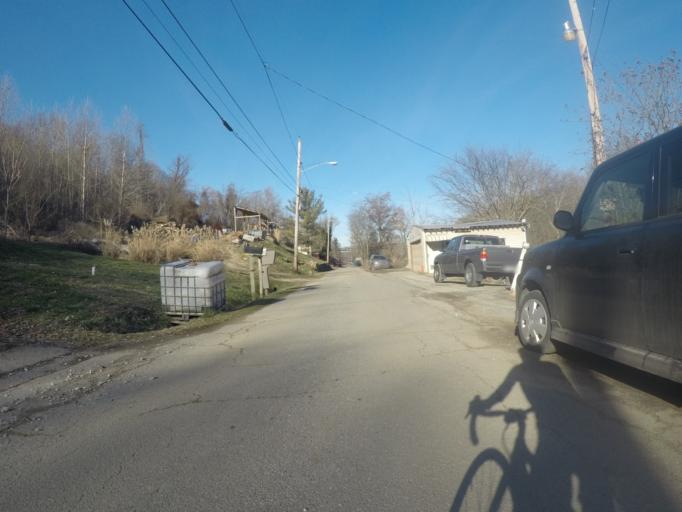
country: US
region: West Virginia
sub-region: Cabell County
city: Huntington
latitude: 38.3966
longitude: -82.4876
